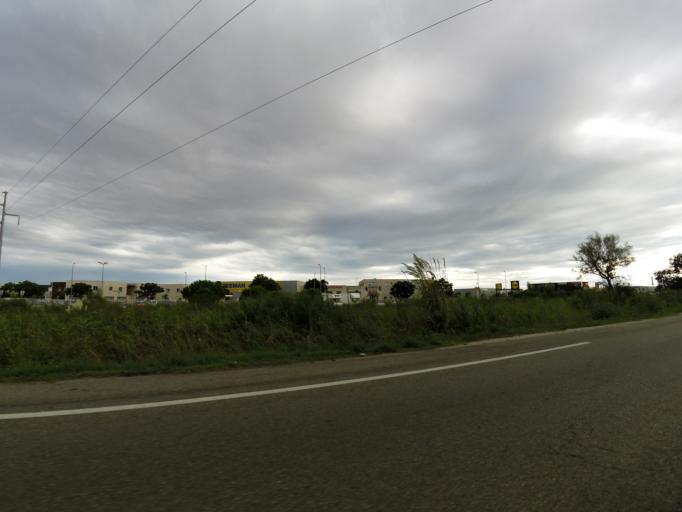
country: FR
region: Languedoc-Roussillon
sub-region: Departement du Gard
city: Aigues-Mortes
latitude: 43.5789
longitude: 4.1883
